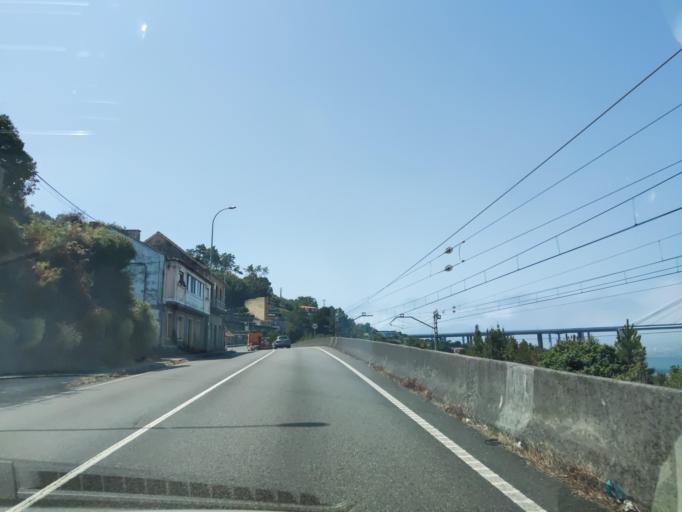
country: ES
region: Galicia
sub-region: Provincia de Pontevedra
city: Redondela
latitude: 42.2855
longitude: -8.6526
